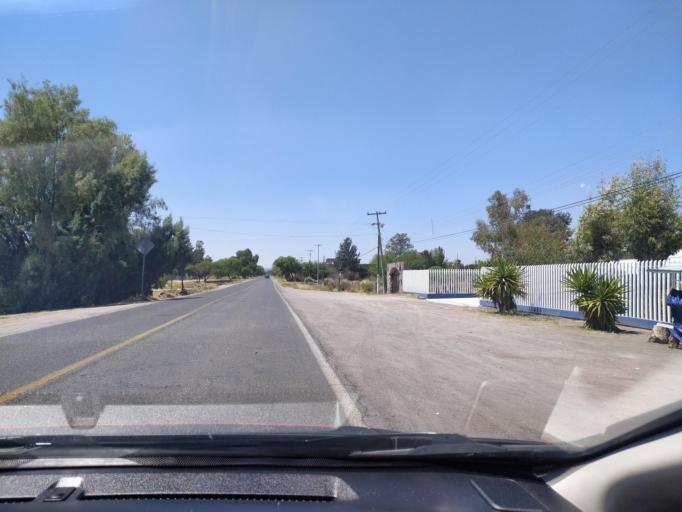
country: MX
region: Guanajuato
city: Ciudad Manuel Doblado
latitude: 20.7413
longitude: -101.8852
